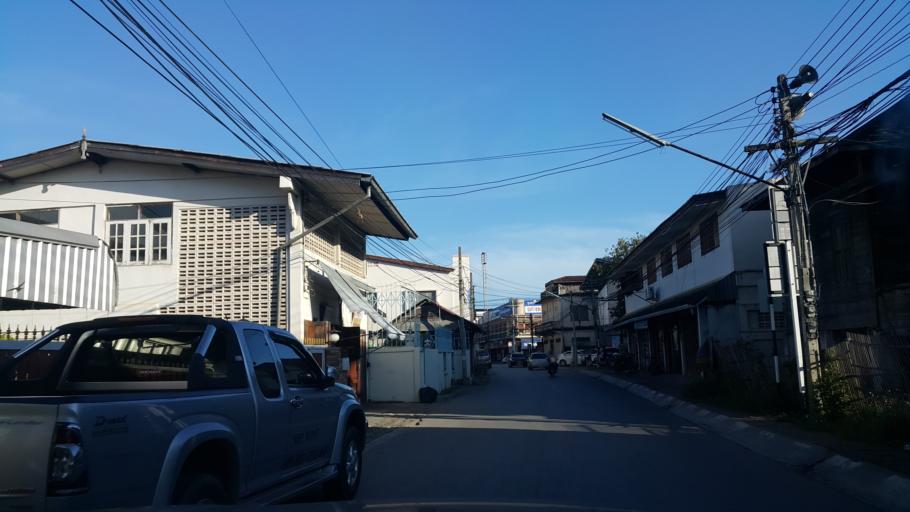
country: TH
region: Lamphun
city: Lamphun
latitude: 18.5777
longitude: 99.0051
